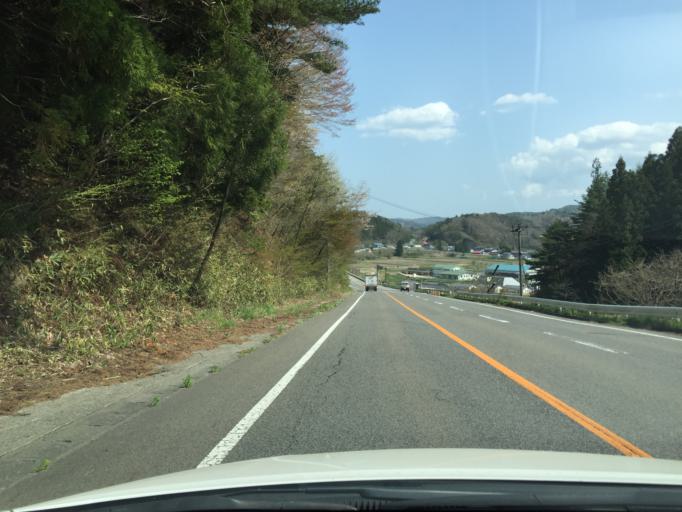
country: JP
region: Fukushima
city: Funehikimachi-funehiki
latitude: 37.4417
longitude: 140.7905
